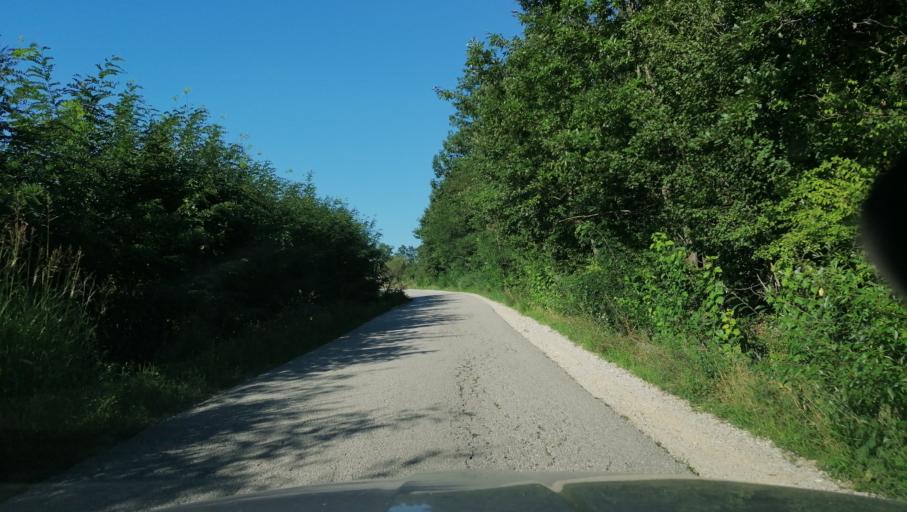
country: RS
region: Central Serbia
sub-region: Sumadijski Okrug
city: Knic
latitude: 43.8648
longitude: 20.6036
